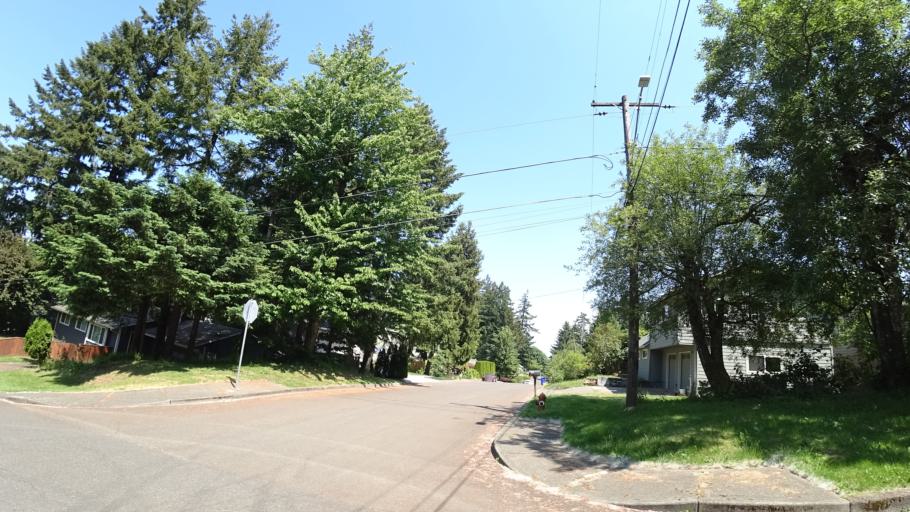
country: US
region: Oregon
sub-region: Washington County
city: Metzger
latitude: 45.4425
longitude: -122.7231
